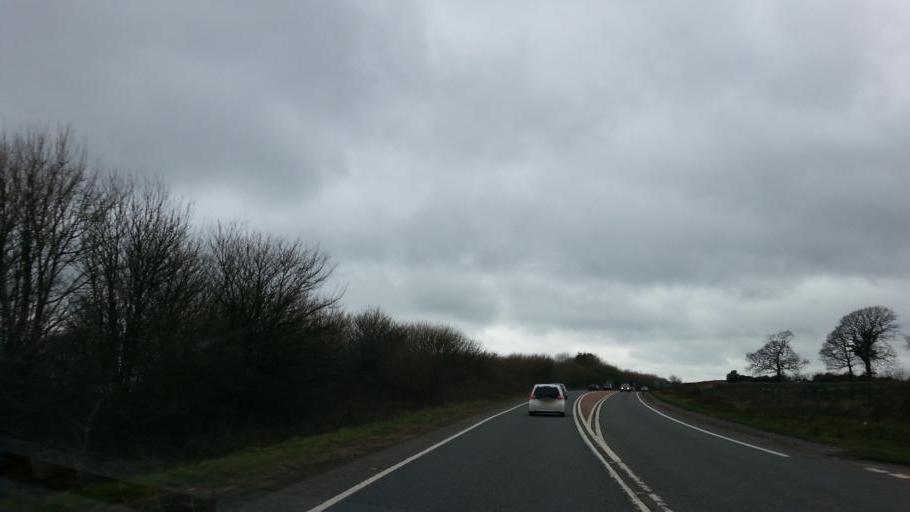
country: GB
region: England
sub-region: Devon
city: South Molton
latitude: 50.9827
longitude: -3.6945
